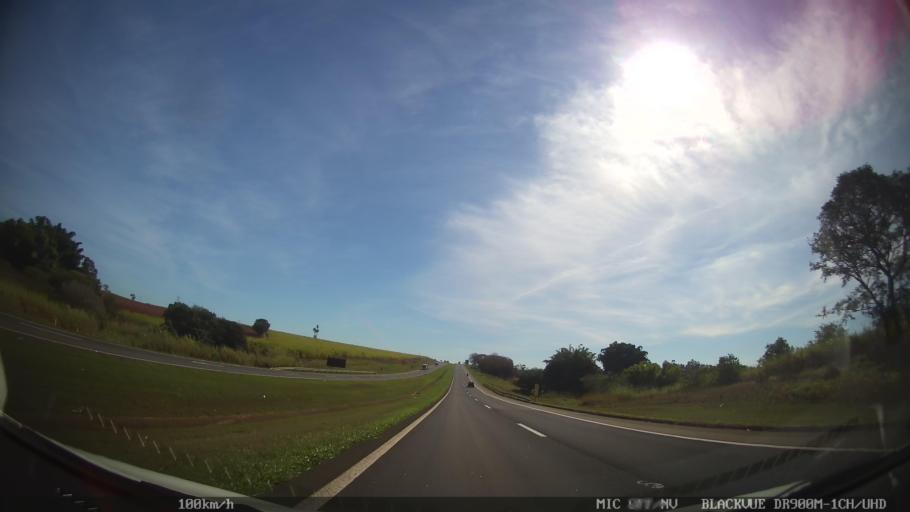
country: BR
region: Sao Paulo
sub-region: Leme
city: Leme
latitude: -22.1161
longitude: -47.4119
